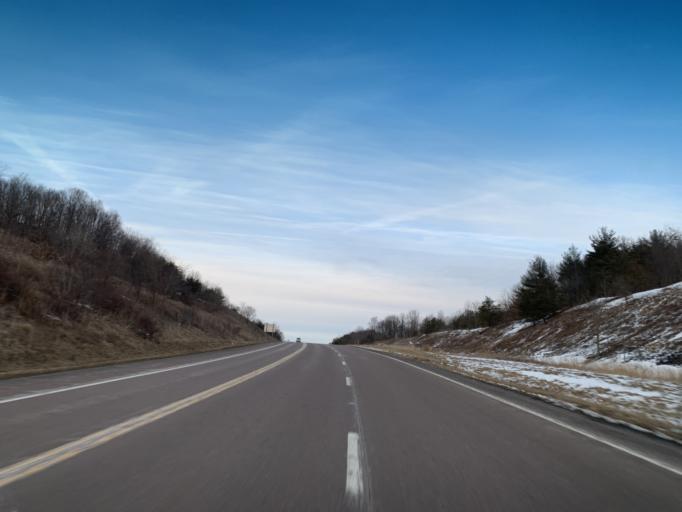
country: US
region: Maryland
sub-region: Allegany County
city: Cumberland
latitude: 39.6984
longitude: -78.7076
